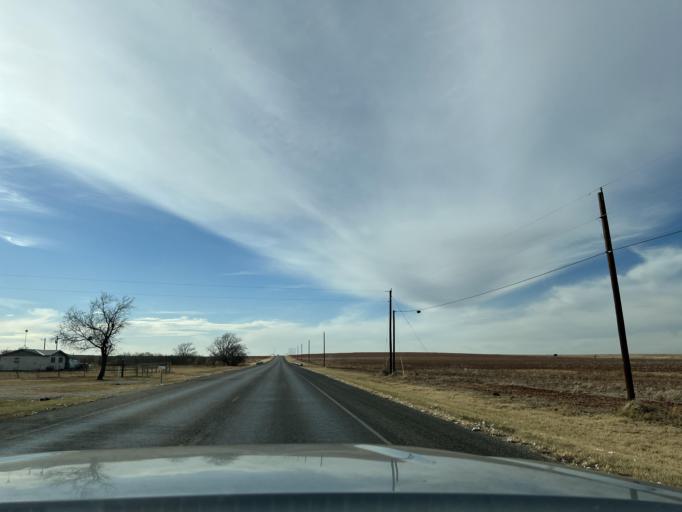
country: US
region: Texas
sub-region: Fisher County
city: Roby
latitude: 32.7408
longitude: -100.4817
